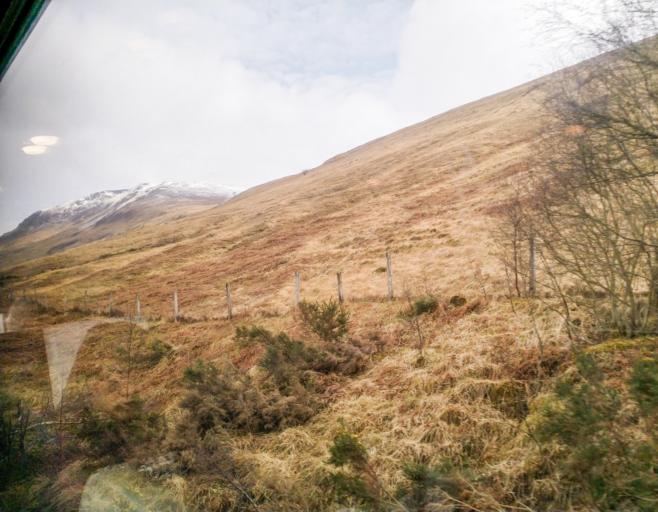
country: GB
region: Scotland
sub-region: Highland
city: Spean Bridge
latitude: 56.8059
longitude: -4.7186
